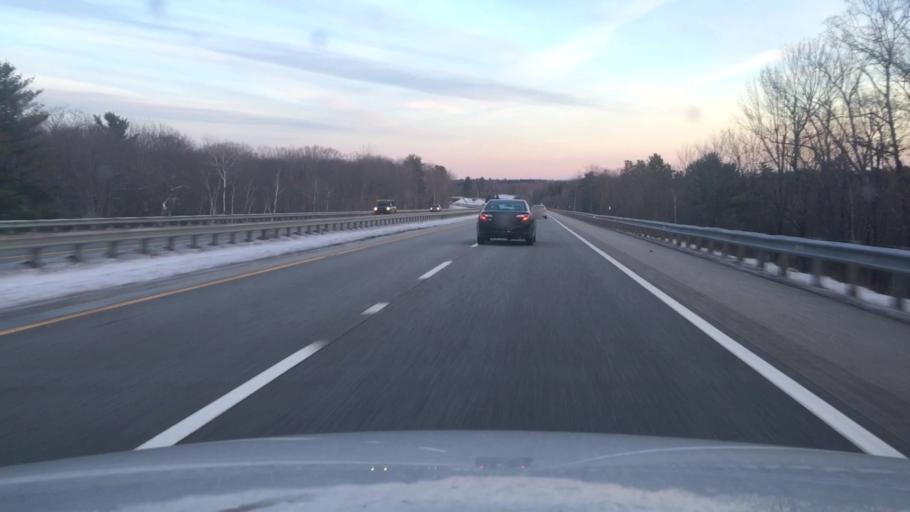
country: US
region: Maine
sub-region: Kennebec County
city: Monmouth
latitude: 44.1251
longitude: -69.9784
